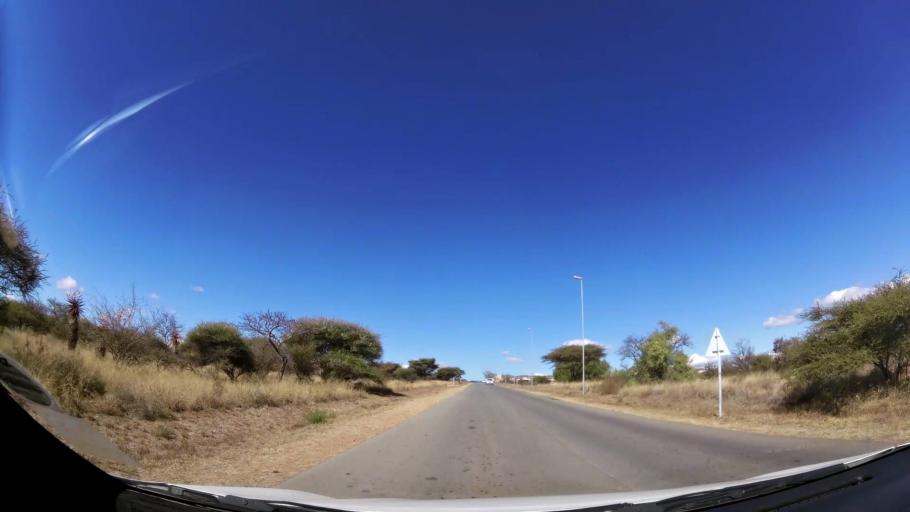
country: ZA
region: Limpopo
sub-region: Capricorn District Municipality
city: Polokwane
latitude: -23.8833
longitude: 29.5103
